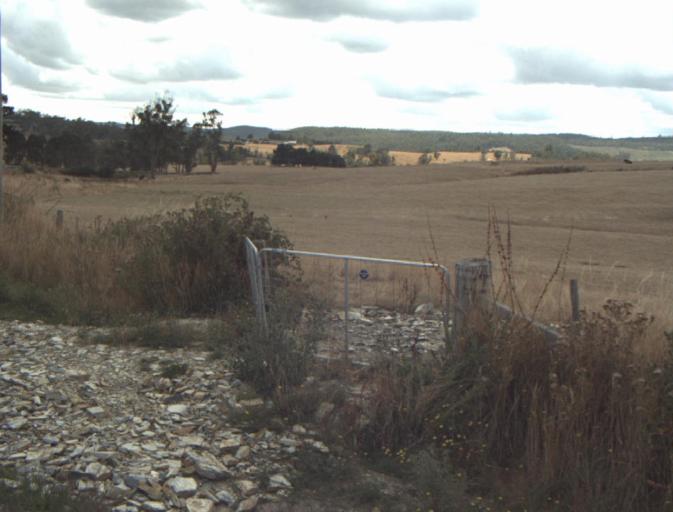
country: AU
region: Tasmania
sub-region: Launceston
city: Mayfield
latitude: -41.2117
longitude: 147.1086
